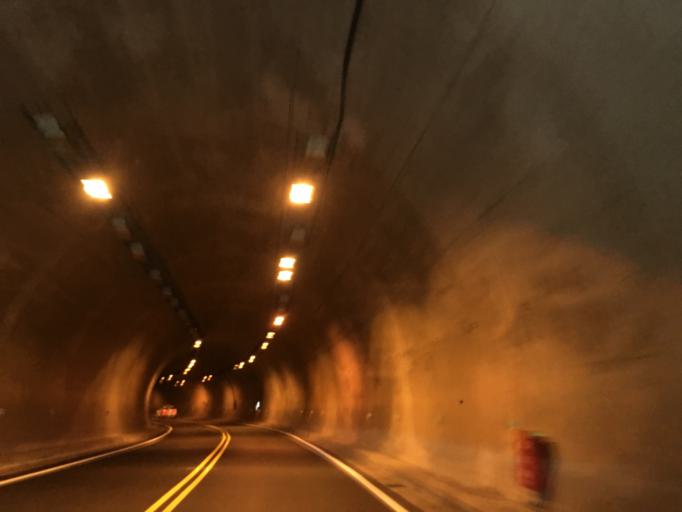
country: TW
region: Taiwan
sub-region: Hualien
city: Hualian
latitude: 24.1712
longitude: 121.5608
